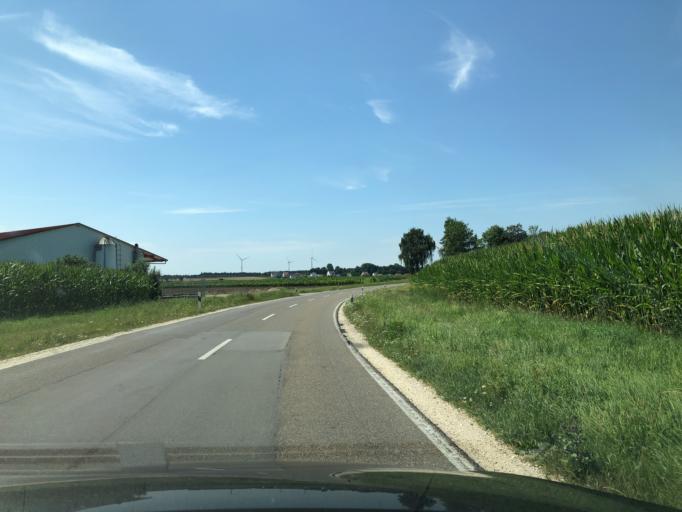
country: DE
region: Bavaria
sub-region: Swabia
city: Allmannshofen
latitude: 48.6324
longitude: 10.7610
